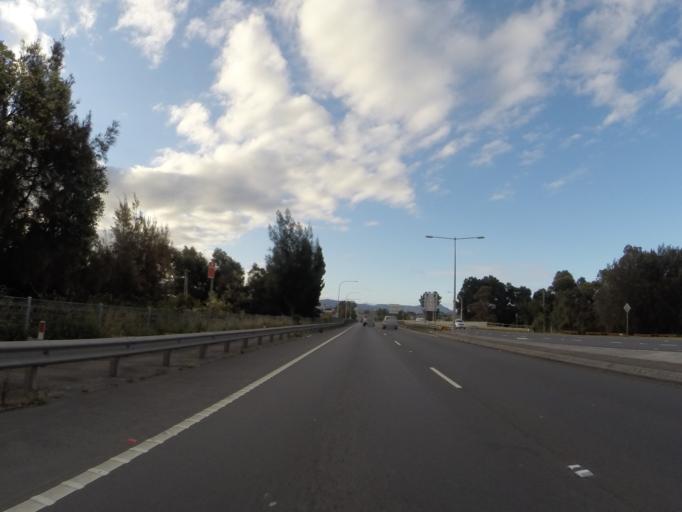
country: AU
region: New South Wales
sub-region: Shellharbour
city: Albion Park Rail
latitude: -34.5474
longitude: 150.7851
